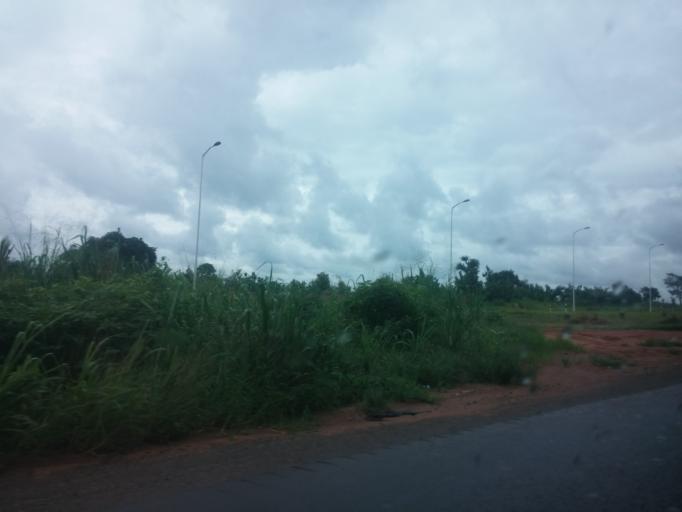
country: TG
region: Maritime
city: Tsevie
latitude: 6.3529
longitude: 1.2118
